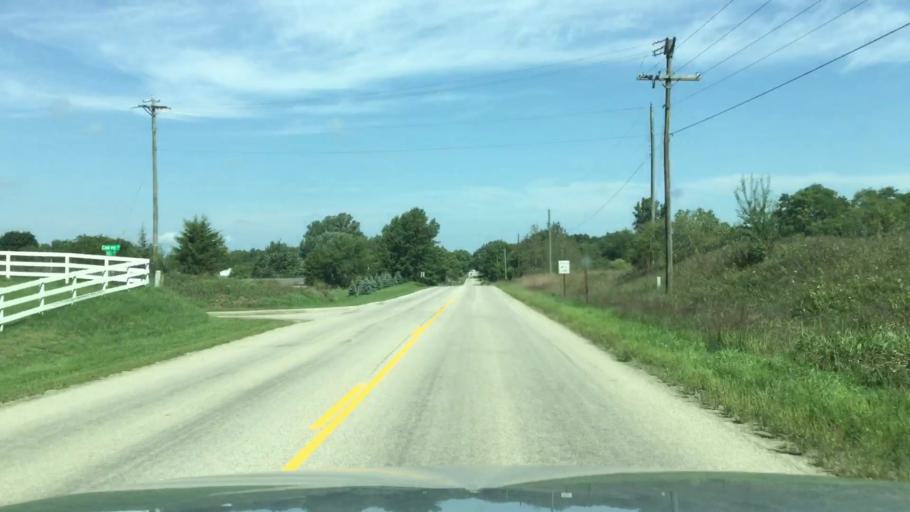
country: US
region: Michigan
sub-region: Lenawee County
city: Manitou Beach-Devils Lake
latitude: 42.0336
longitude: -84.2763
